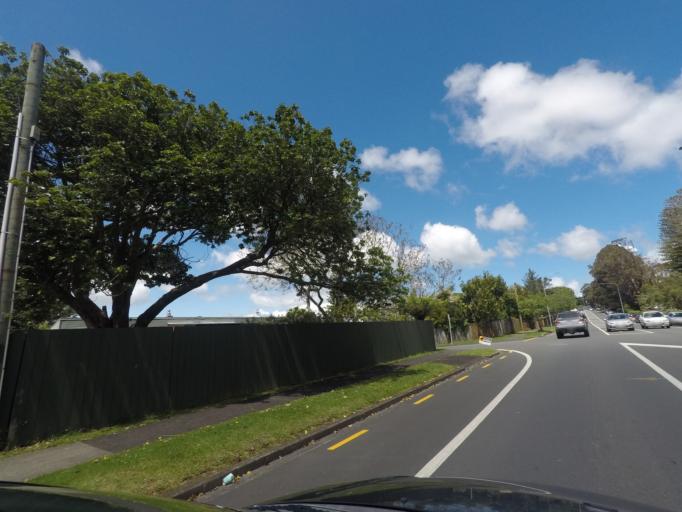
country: NZ
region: Auckland
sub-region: Auckland
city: Waitakere
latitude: -36.9033
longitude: 174.6545
